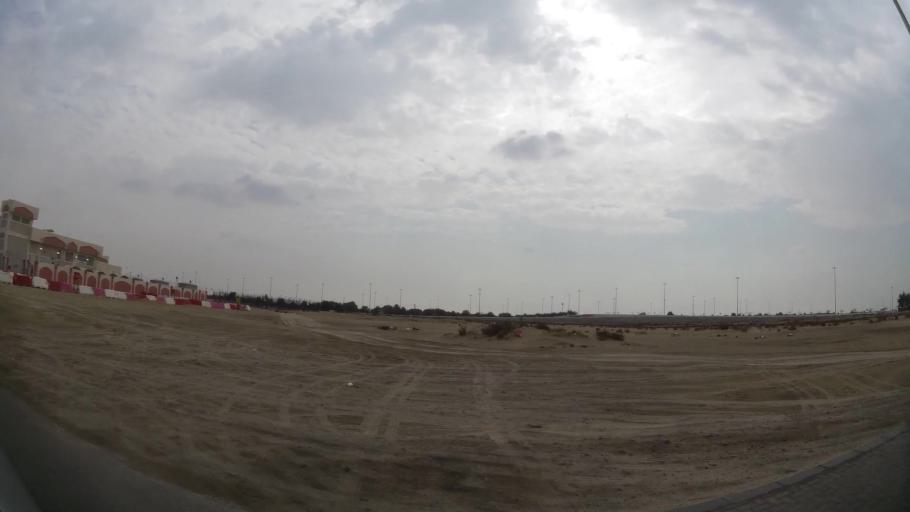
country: AE
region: Abu Dhabi
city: Abu Dhabi
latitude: 24.6267
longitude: 54.7128
